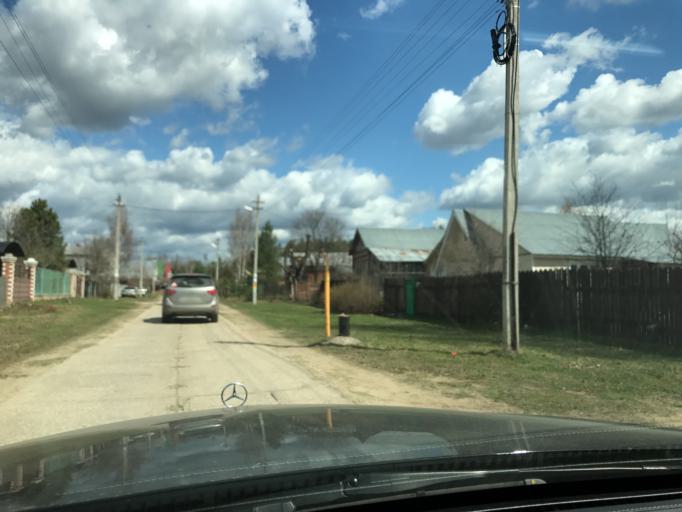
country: RU
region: Vladimir
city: Pokrov
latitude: 55.8563
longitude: 39.2010
